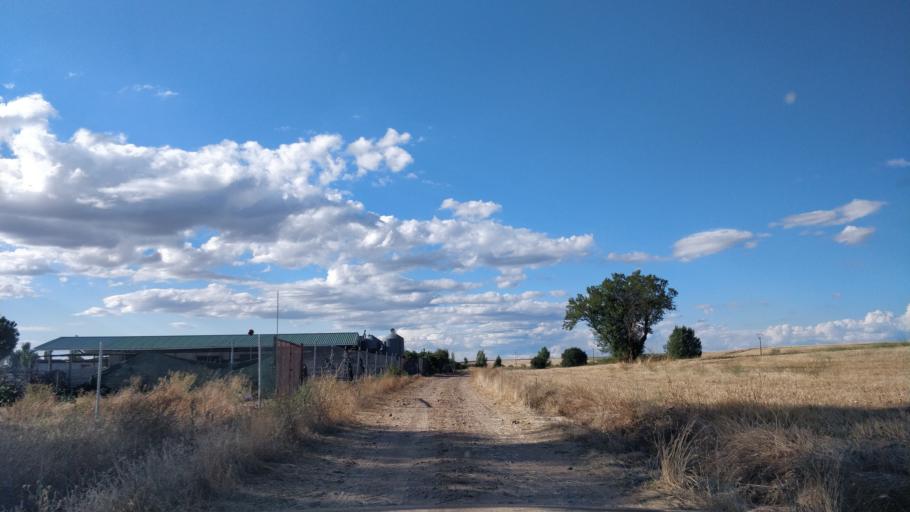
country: ES
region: Castille and Leon
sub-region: Provincia de Leon
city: Valverde-Enrique
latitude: 42.3284
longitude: -5.2795
